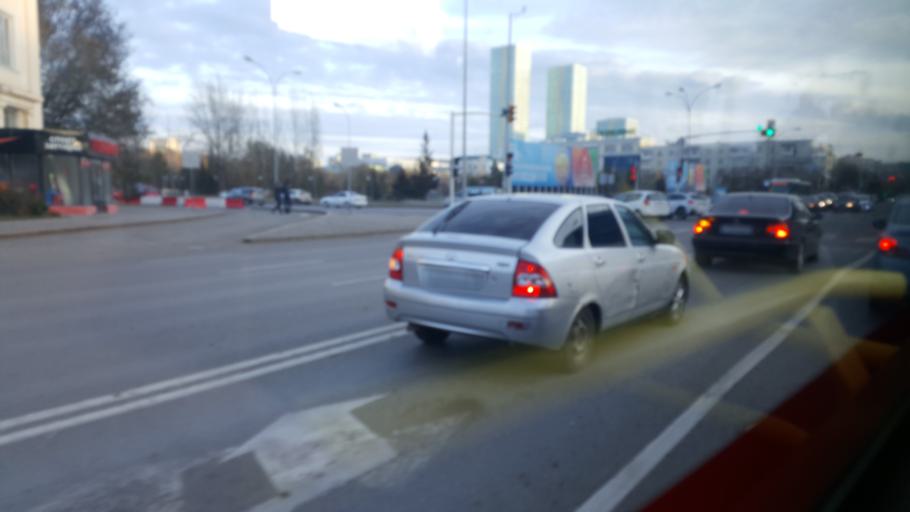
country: KZ
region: Astana Qalasy
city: Astana
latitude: 51.1672
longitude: 71.4137
